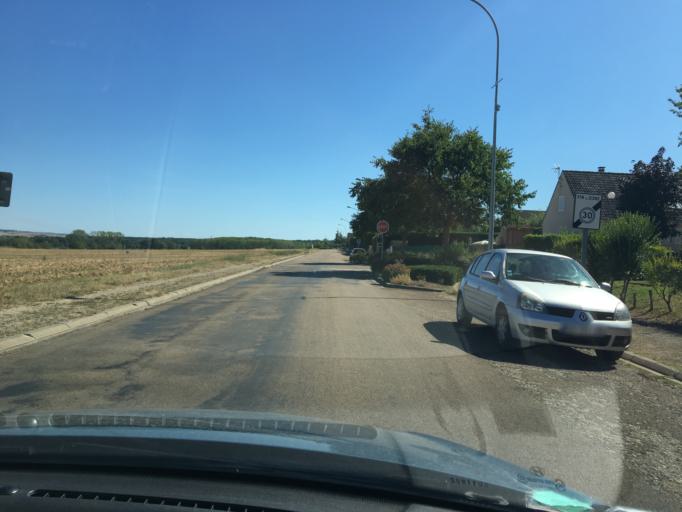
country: FR
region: Bourgogne
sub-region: Departement de l'Yonne
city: Appoigny
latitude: 47.8727
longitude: 3.5200
